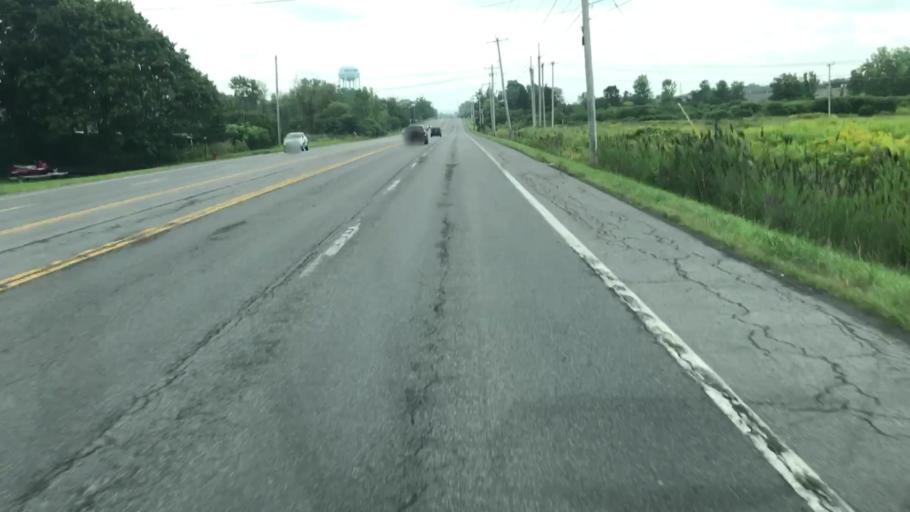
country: US
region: New York
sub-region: Onondaga County
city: Liverpool
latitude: 43.1283
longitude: -76.1865
